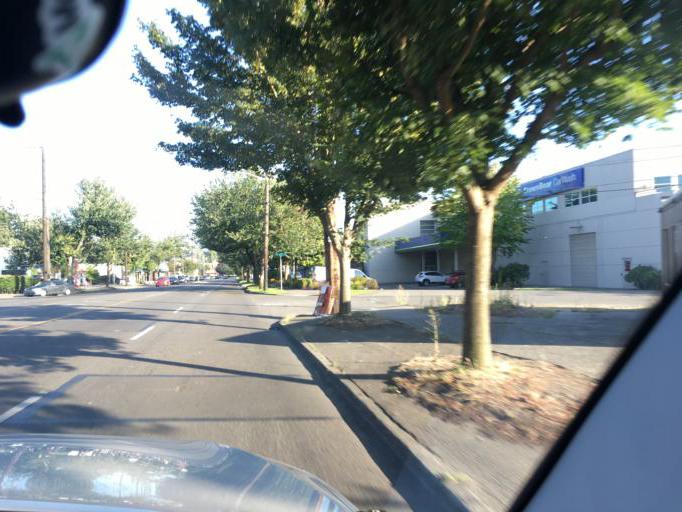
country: US
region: Washington
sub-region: King County
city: Seattle
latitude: 47.6564
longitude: -122.3624
